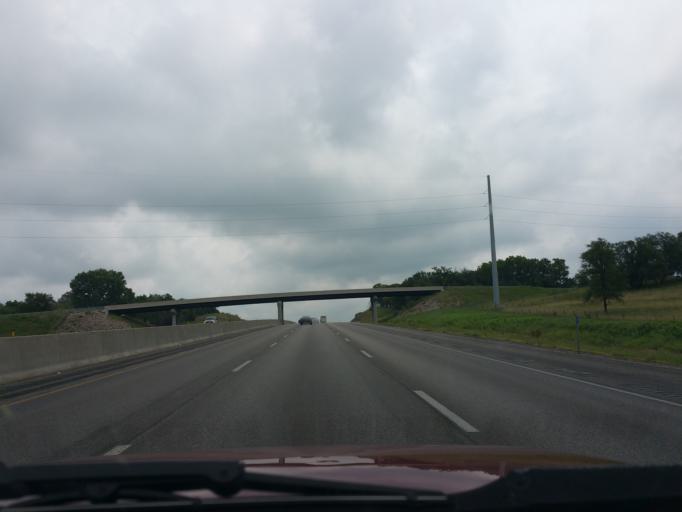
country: US
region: Kansas
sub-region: Shawnee County
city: Topeka
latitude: 39.0276
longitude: -95.5594
